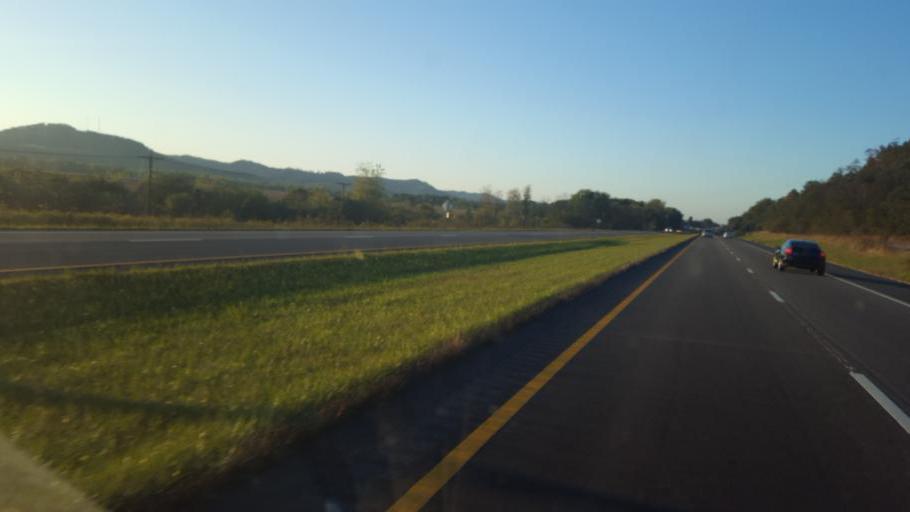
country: US
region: Ohio
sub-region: Scioto County
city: Lucasville
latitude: 38.8613
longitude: -82.9898
